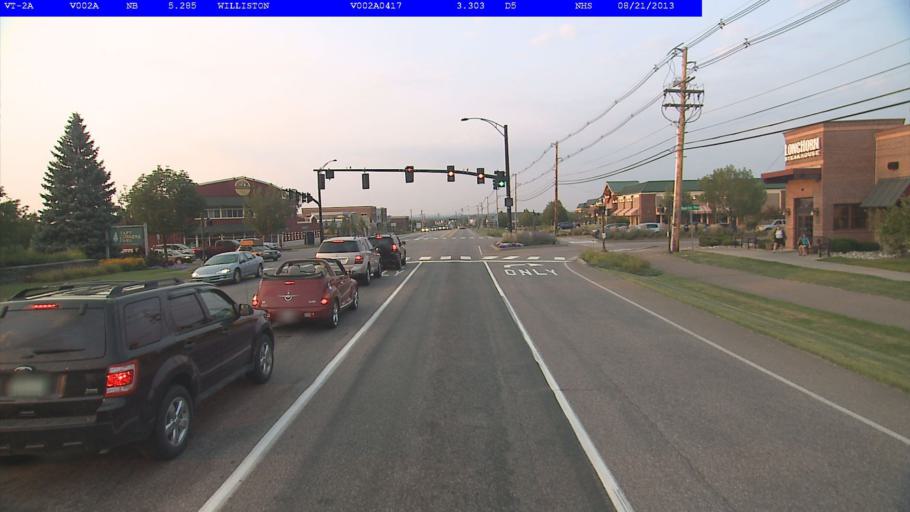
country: US
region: Vermont
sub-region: Chittenden County
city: Williston
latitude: 44.4437
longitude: -73.1126
